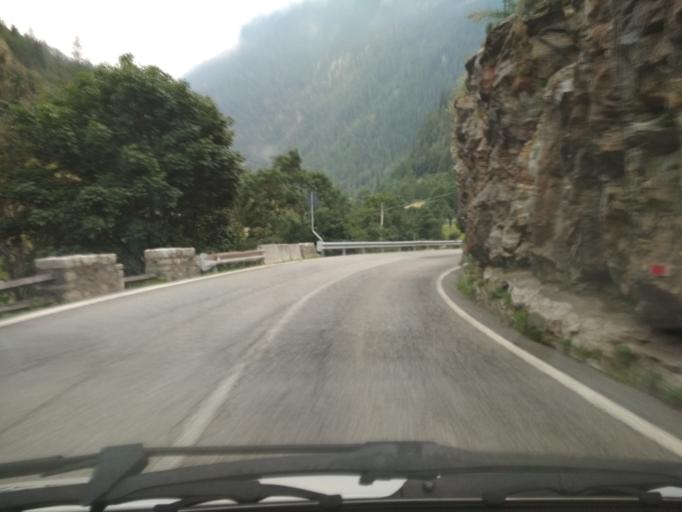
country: IT
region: Aosta Valley
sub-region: Valle d'Aosta
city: Gaby
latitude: 45.7364
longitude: 7.8543
